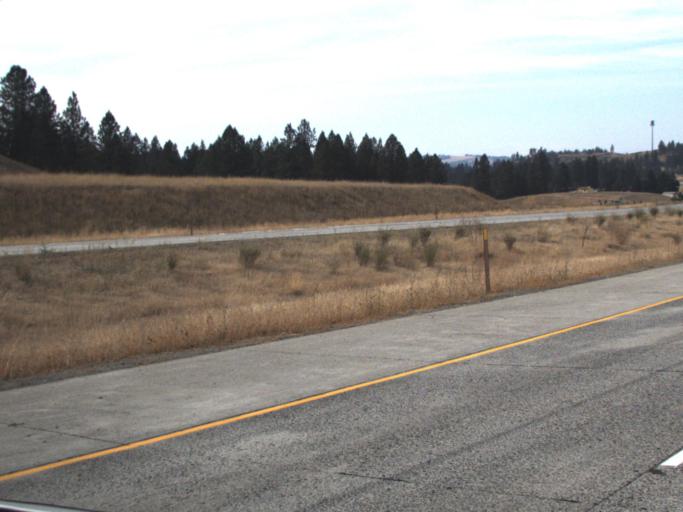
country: US
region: Washington
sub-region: Spokane County
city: Mead
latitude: 47.7704
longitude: -117.3683
